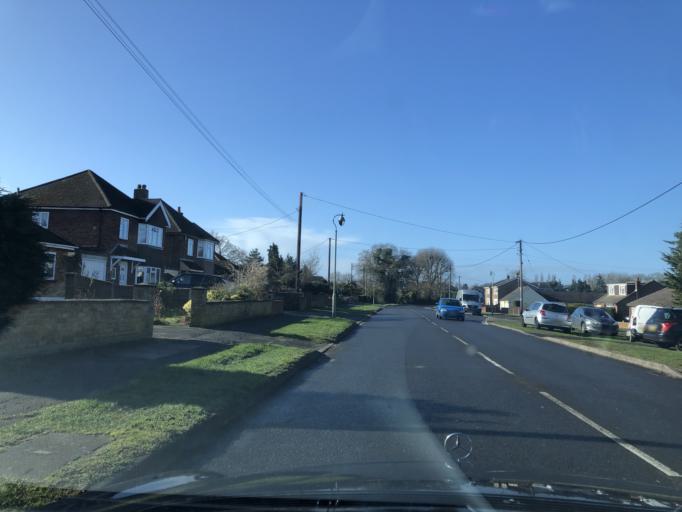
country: GB
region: England
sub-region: Hampshire
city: Farnborough
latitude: 51.2937
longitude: -0.7314
